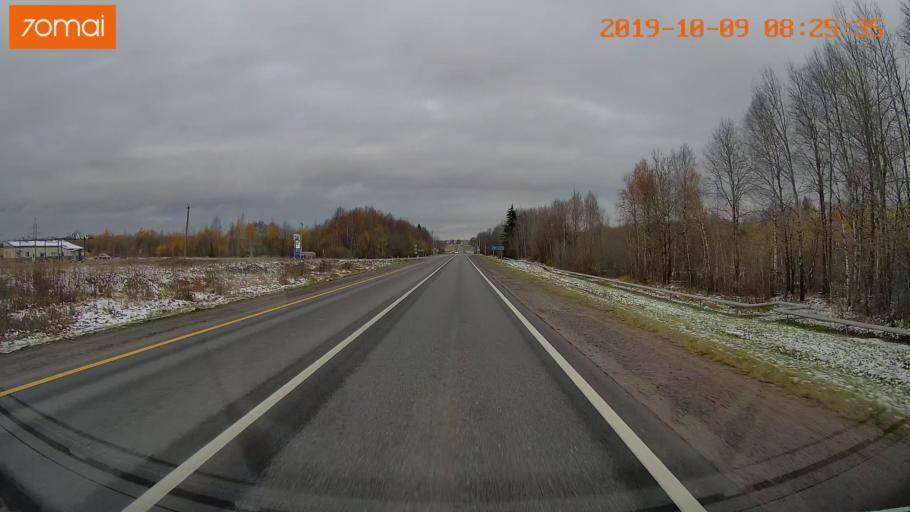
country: RU
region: Vologda
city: Gryazovets
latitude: 58.7831
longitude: 40.2715
